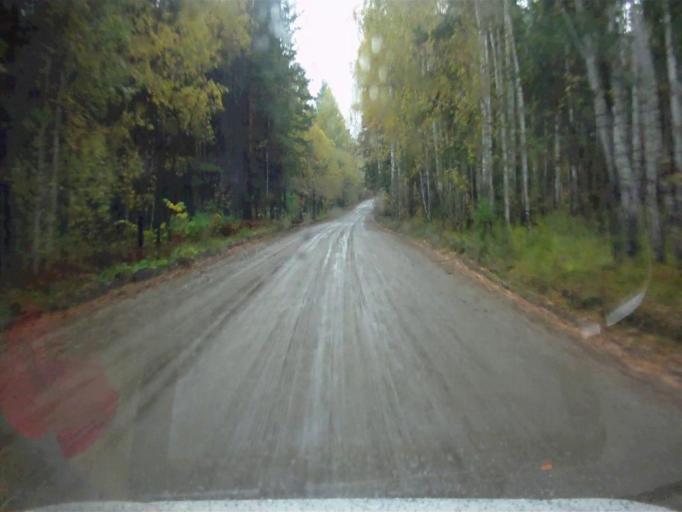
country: RU
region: Chelyabinsk
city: Kyshtym
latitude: 55.8875
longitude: 60.4650
